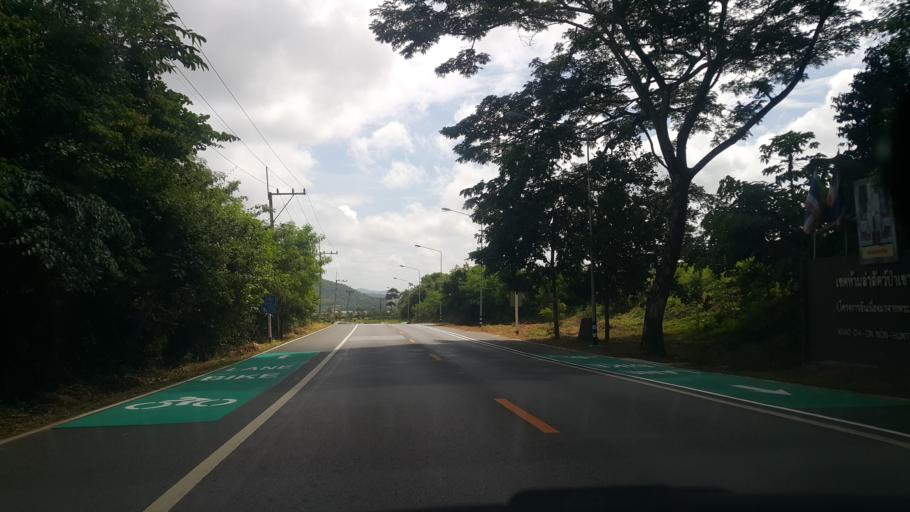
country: TH
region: Rayong
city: Ban Chang
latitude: 12.7602
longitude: 100.9731
